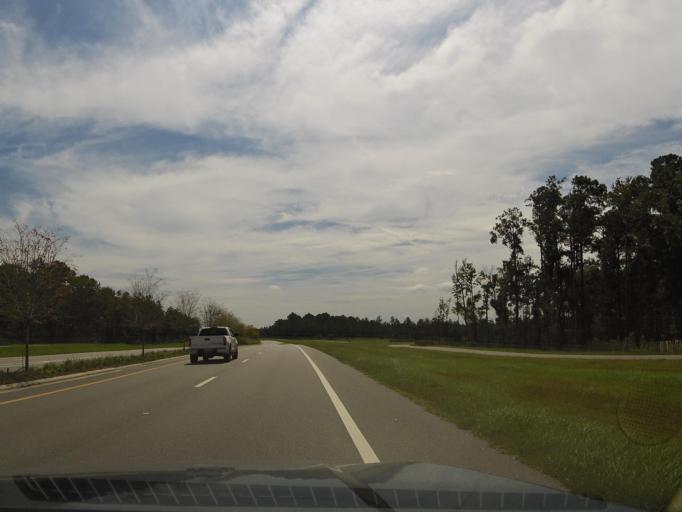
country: US
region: Florida
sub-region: Saint Johns County
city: Fruit Cove
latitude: 30.0269
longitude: -81.5233
